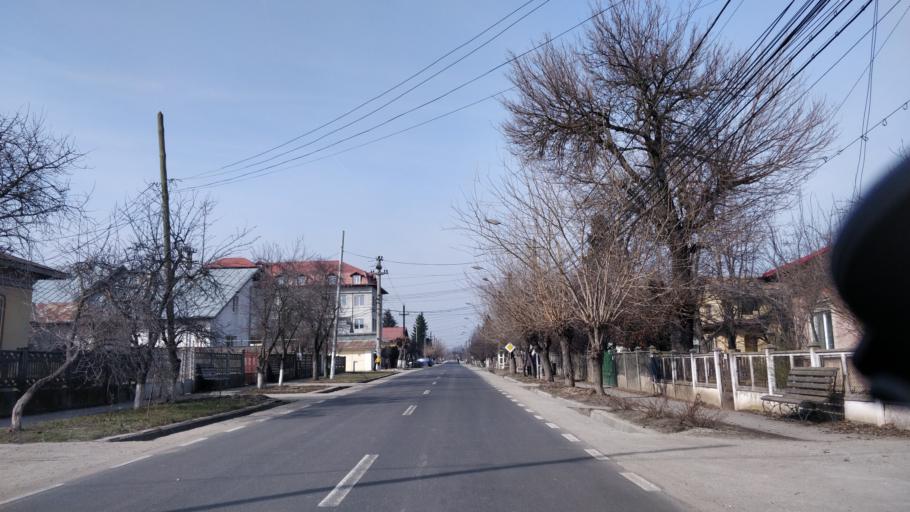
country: RO
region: Giurgiu
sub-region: Comuna Bolintin Deal
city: Bolintin Deal
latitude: 44.4570
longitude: 25.8189
